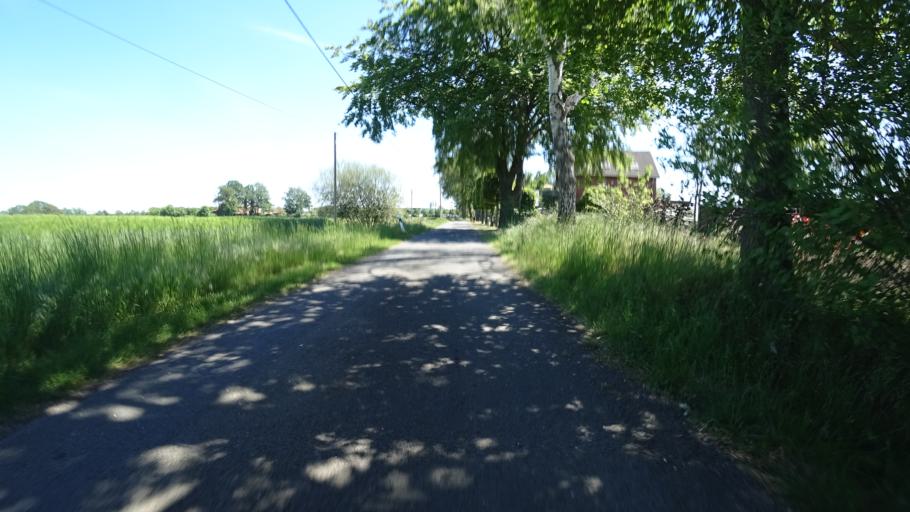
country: DE
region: North Rhine-Westphalia
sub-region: Regierungsbezirk Detmold
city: Guetersloh
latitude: 51.8596
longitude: 8.3611
